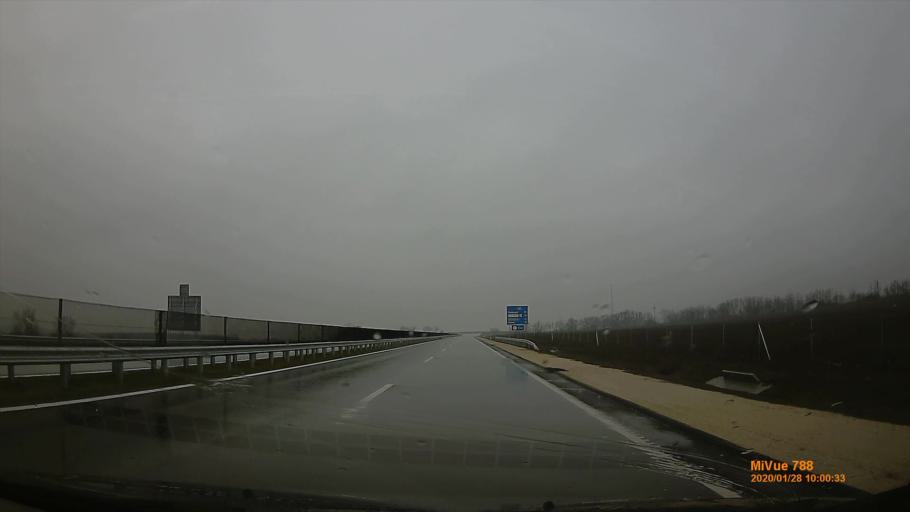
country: HU
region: Pest
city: Albertirsa
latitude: 47.2655
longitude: 19.6142
